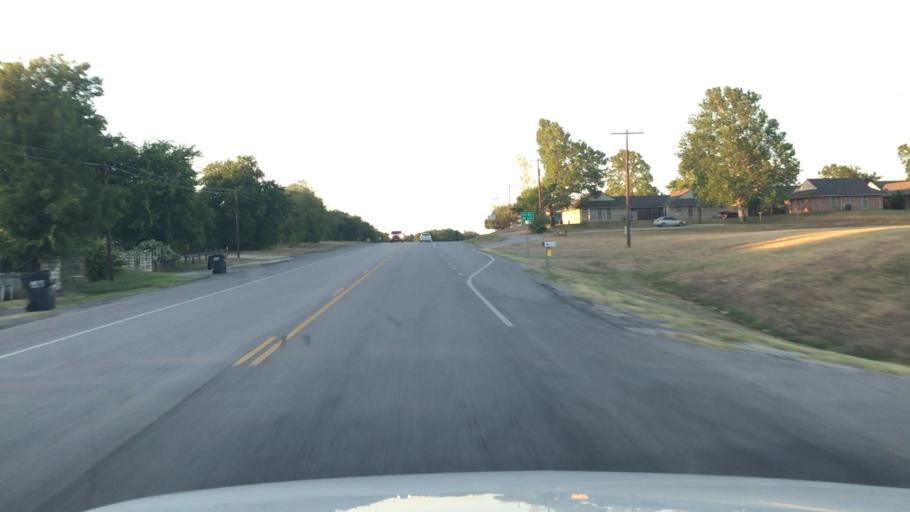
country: US
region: Texas
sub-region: Hamilton County
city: Hico
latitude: 31.9914
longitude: -98.0262
